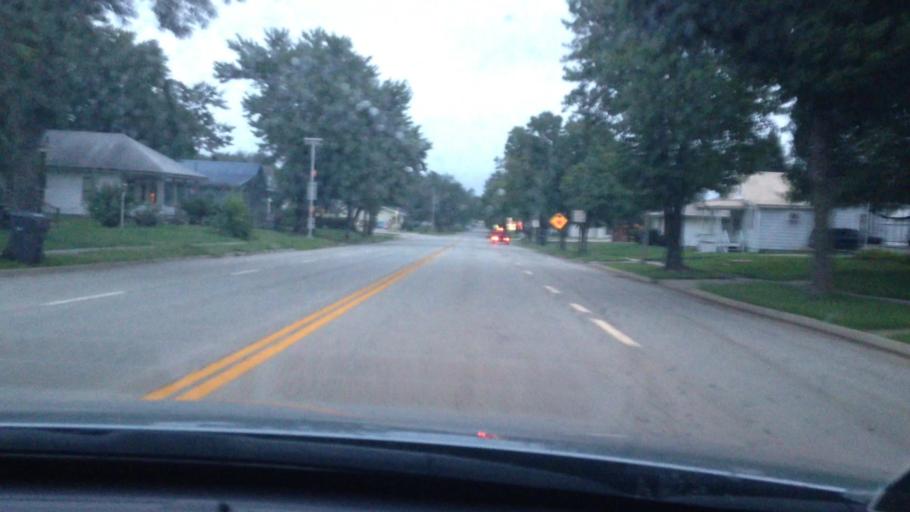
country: US
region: Kansas
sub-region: Brown County
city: Horton
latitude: 39.6689
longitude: -95.5272
